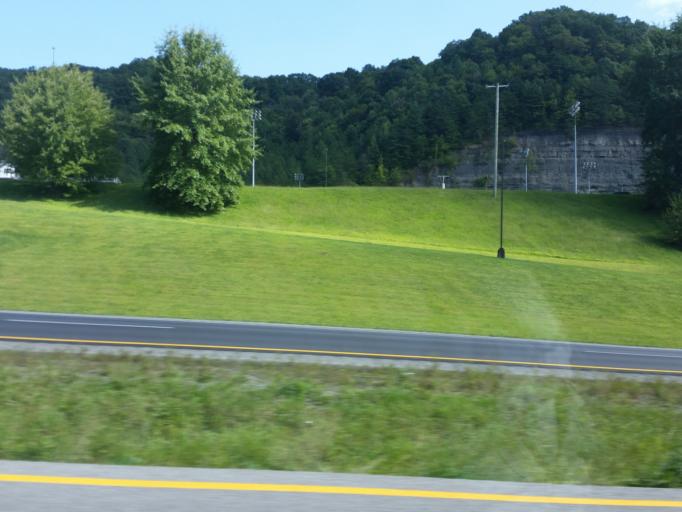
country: US
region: Kentucky
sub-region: Bell County
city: Pineville
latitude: 36.7117
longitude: -83.6939
